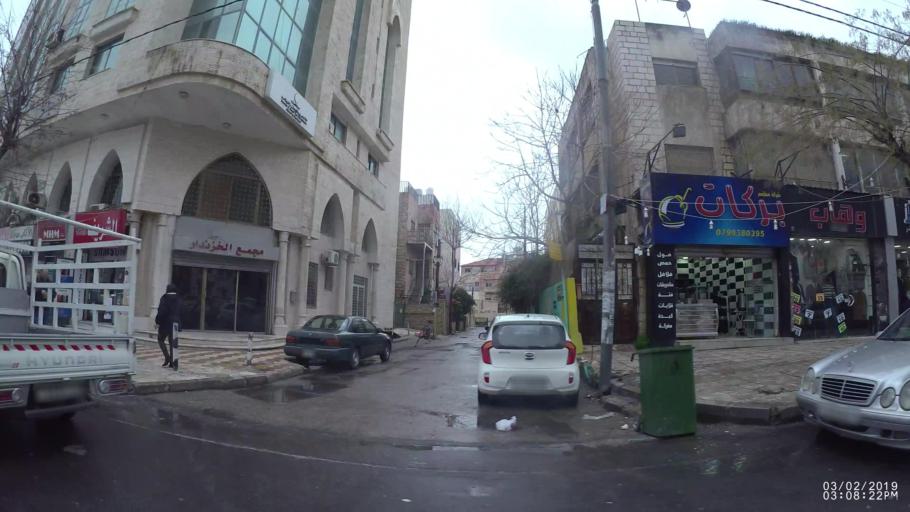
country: JO
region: Amman
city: Amman
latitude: 31.9650
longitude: 35.9214
